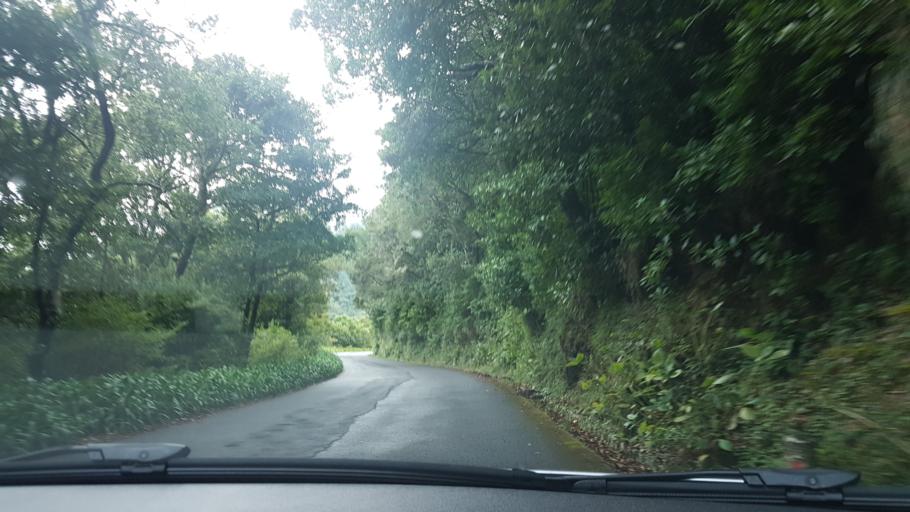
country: PT
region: Madeira
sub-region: Sao Vicente
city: Sao Vicente
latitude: 32.7590
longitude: -17.0178
